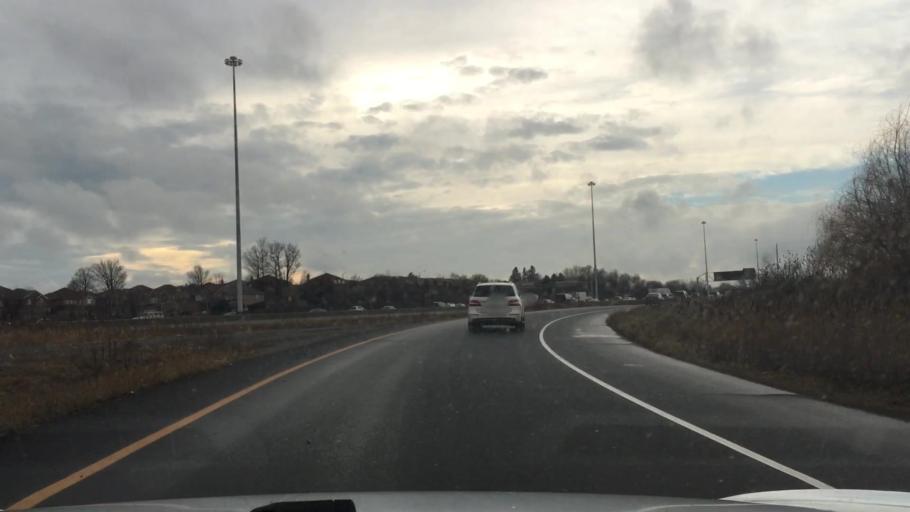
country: CA
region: Ontario
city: Scarborough
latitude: 43.7977
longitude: -79.2005
